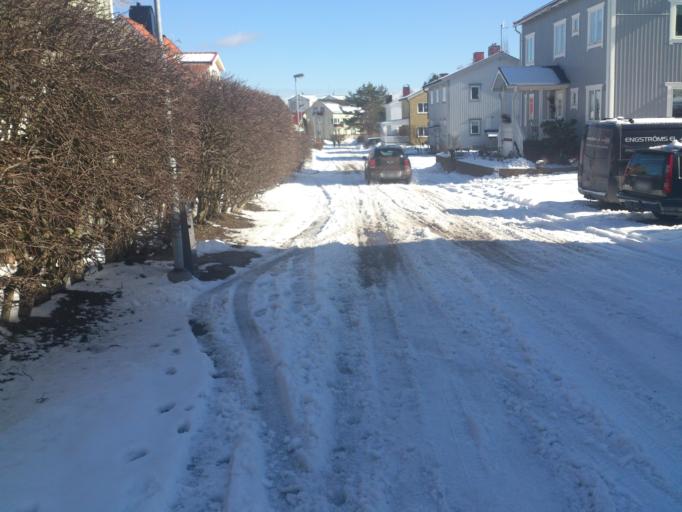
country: SE
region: Vaesternorrland
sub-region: Sundsvalls Kommun
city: Sundsvall
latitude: 62.3804
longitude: 17.3186
